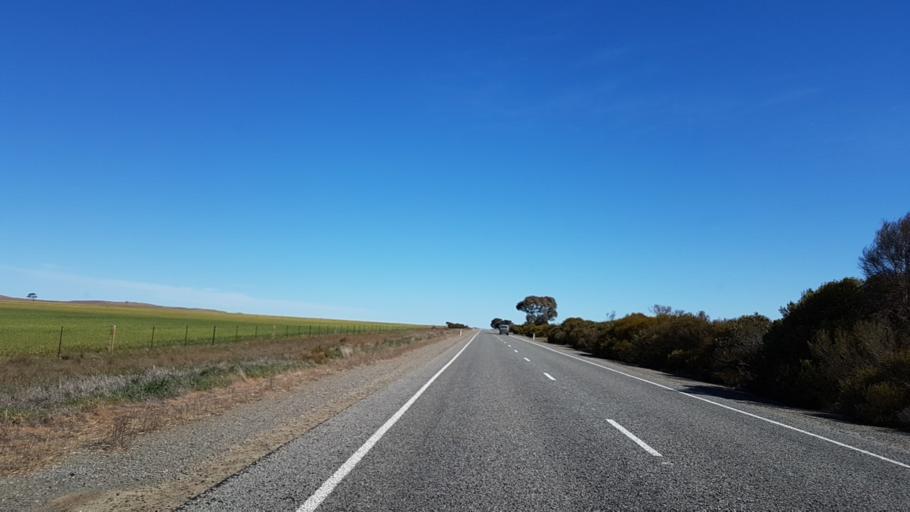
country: AU
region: South Australia
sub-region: Northern Areas
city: Jamestown
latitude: -33.2515
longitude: 138.8725
